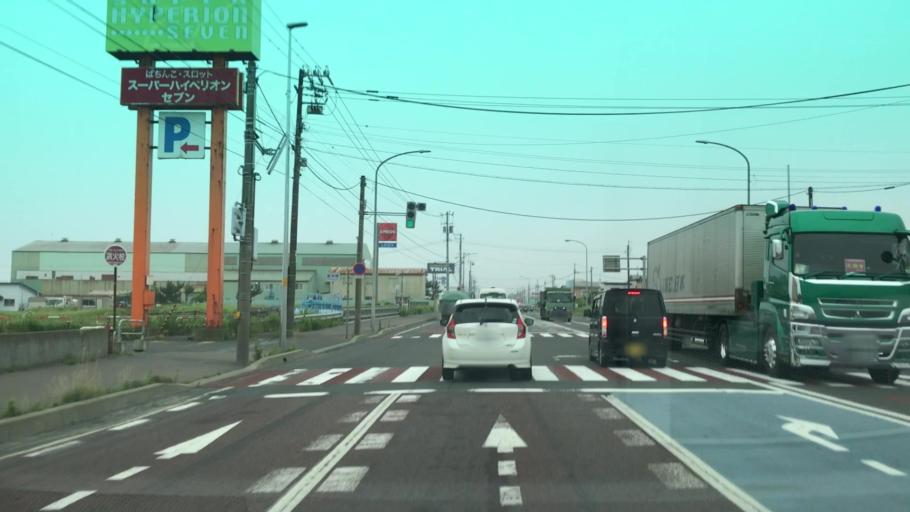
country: JP
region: Hokkaido
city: Muroran
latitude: 42.3821
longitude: 141.0747
